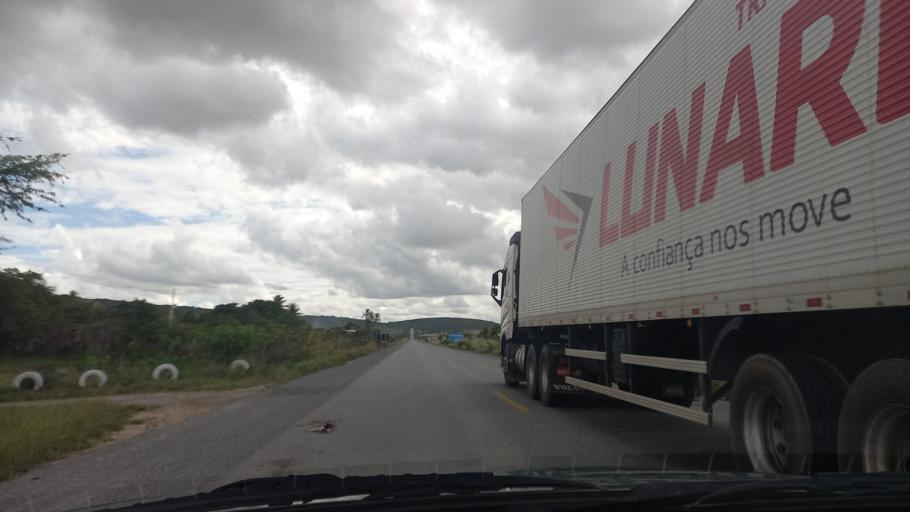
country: BR
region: Pernambuco
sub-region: Lajedo
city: Lajedo
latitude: -8.6680
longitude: -36.3723
